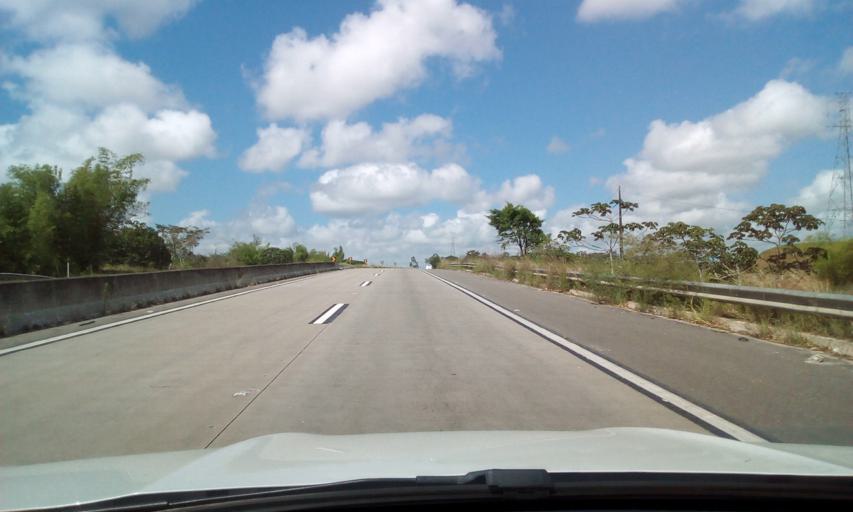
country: BR
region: Paraiba
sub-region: Conde
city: Conde
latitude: -7.3099
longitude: -34.9443
